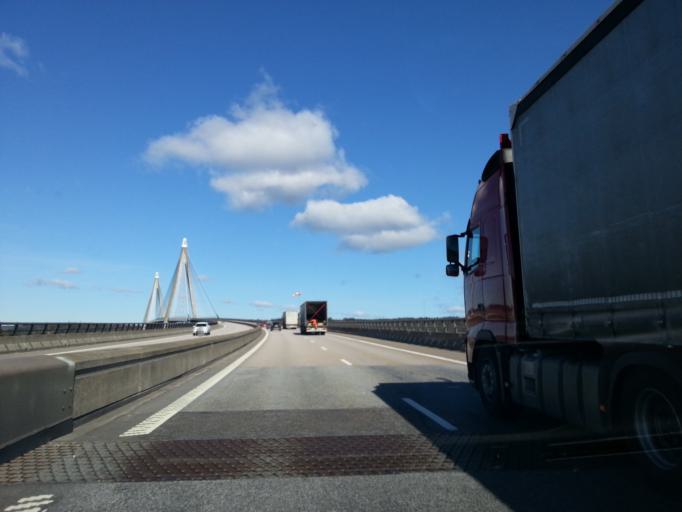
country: SE
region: Vaestra Goetaland
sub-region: Uddevalla Kommun
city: Uddevalla
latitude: 58.3198
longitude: 11.8554
